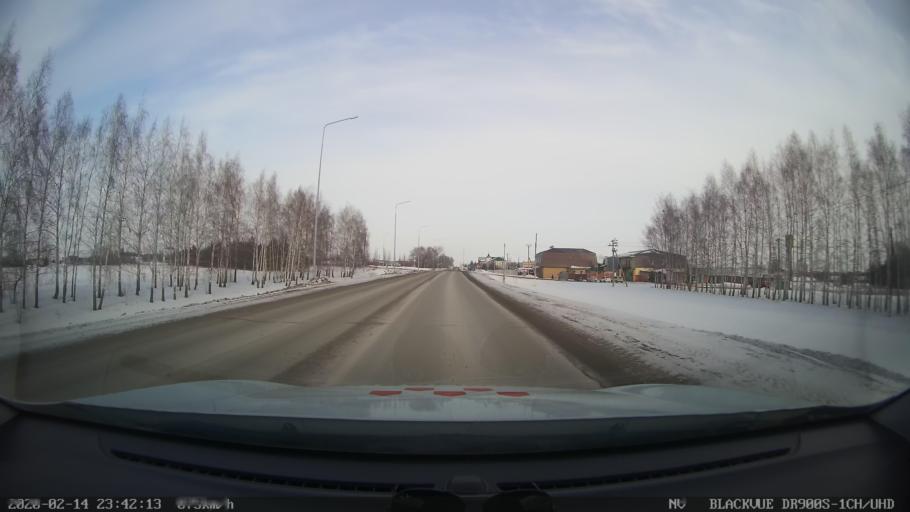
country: RU
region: Tatarstan
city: Kuybyshevskiy Zaton
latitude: 55.1898
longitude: 49.2464
